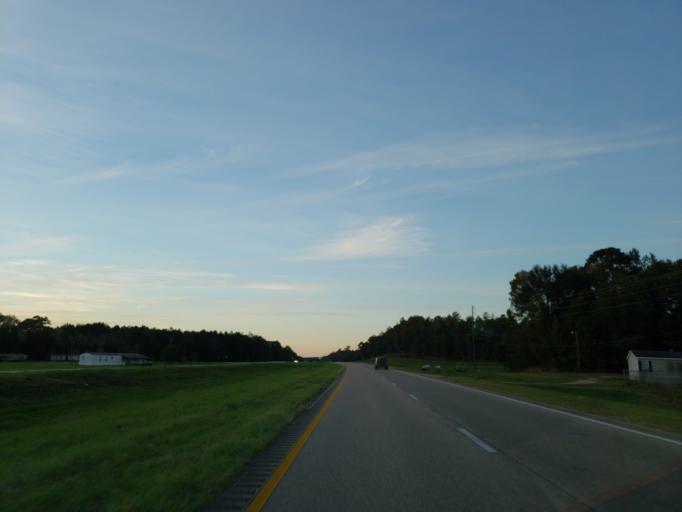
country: US
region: Mississippi
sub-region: Wayne County
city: Belmont
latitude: 31.5798
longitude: -88.5413
